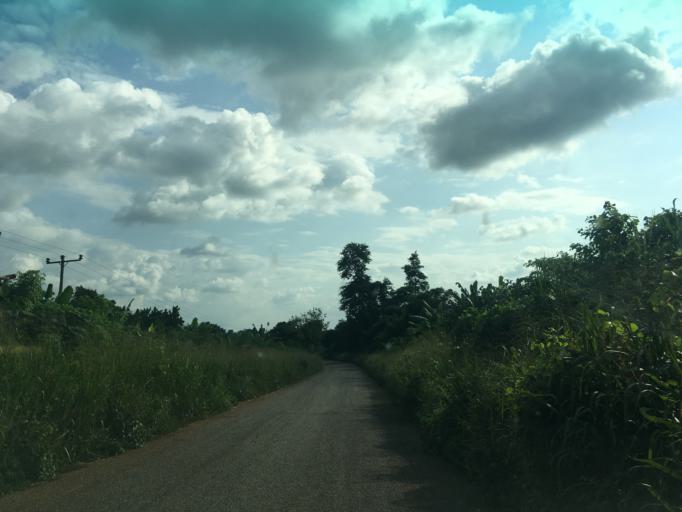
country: GH
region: Western
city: Bibiani
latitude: 6.7870
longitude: -2.5414
